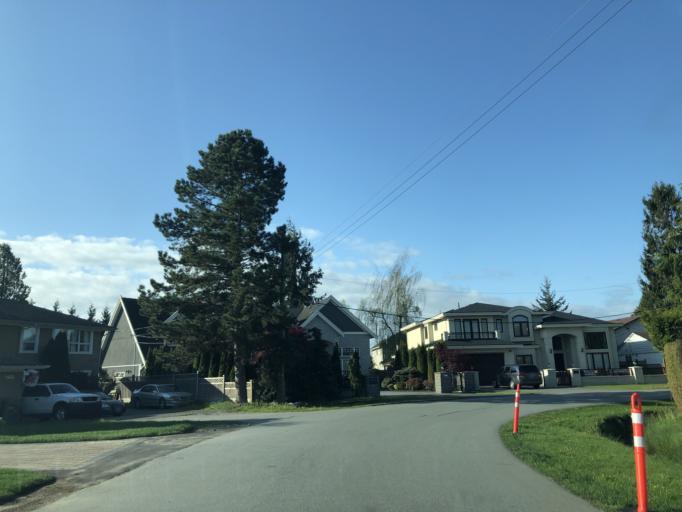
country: CA
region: British Columbia
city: Richmond
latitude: 49.1419
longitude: -123.1154
